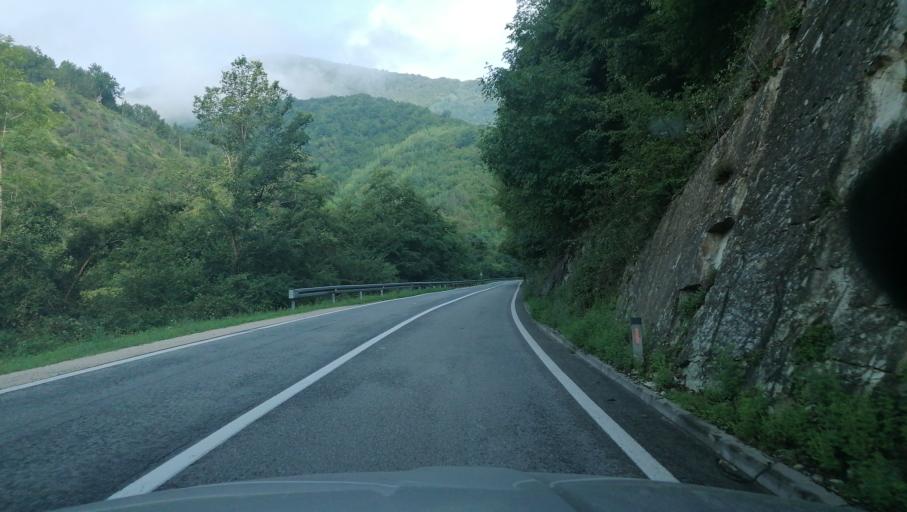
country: BA
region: Federation of Bosnia and Herzegovina
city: Jajce
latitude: 44.2872
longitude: 17.2566
